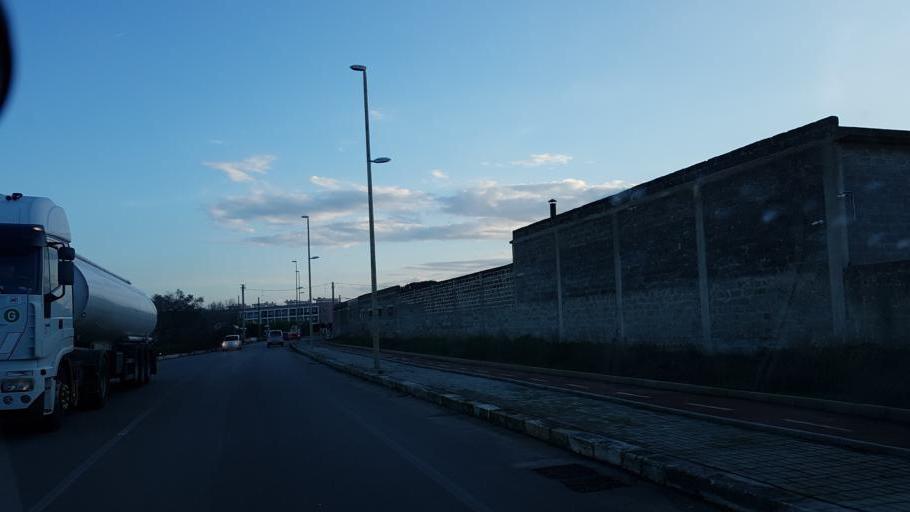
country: IT
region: Apulia
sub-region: Provincia di Lecce
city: Giorgilorio
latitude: 40.3662
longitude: 18.1453
